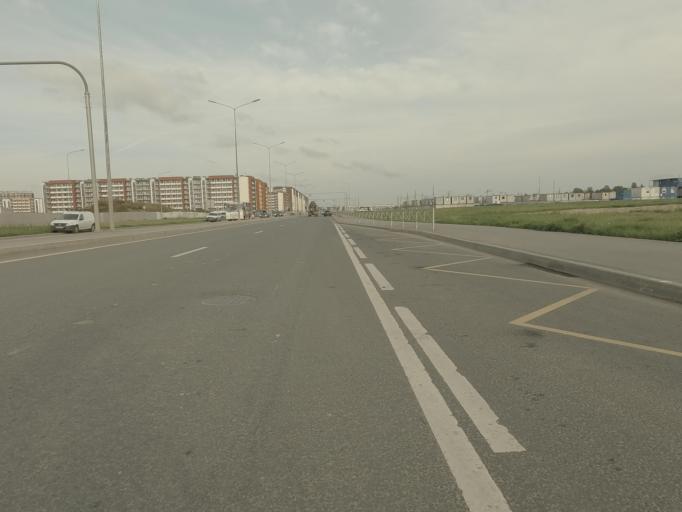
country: RU
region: St.-Petersburg
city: Sosnovaya Polyana
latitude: 59.8403
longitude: 30.0928
